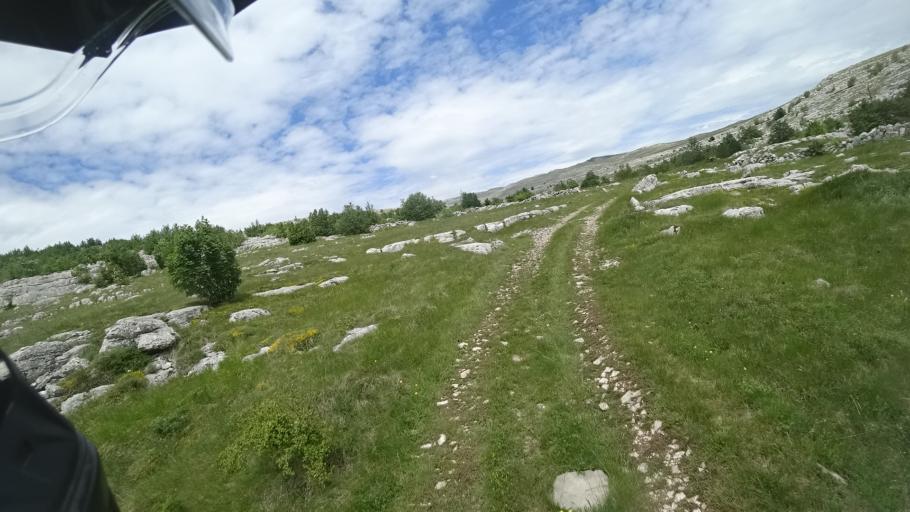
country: HR
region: Splitsko-Dalmatinska
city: Hrvace
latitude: 43.8936
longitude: 16.5859
